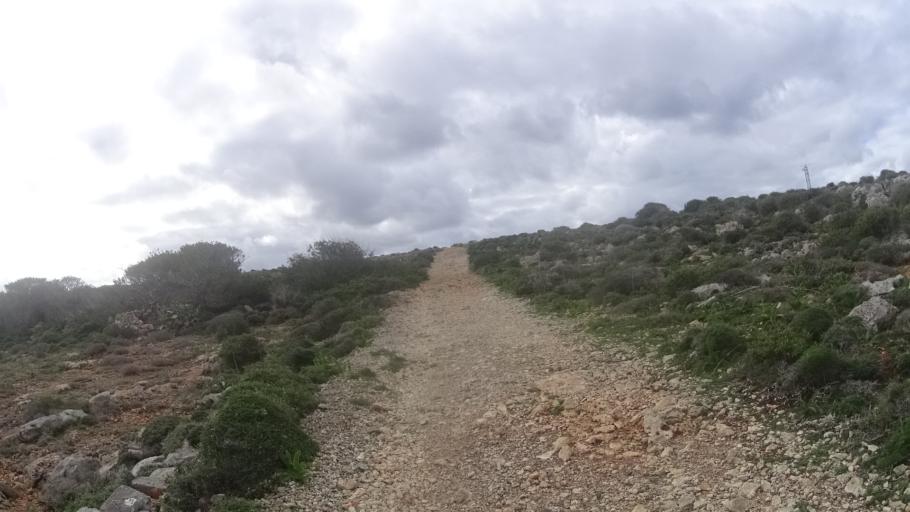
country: MT
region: Il-Mellieha
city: Mellieha
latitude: 35.9740
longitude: 14.3264
